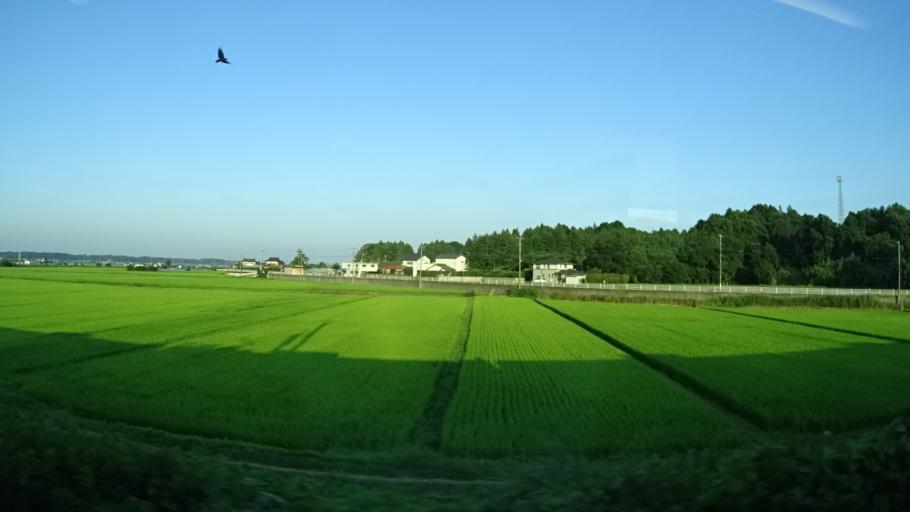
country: JP
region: Ibaraki
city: Ishioka
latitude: 36.1546
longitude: 140.2890
